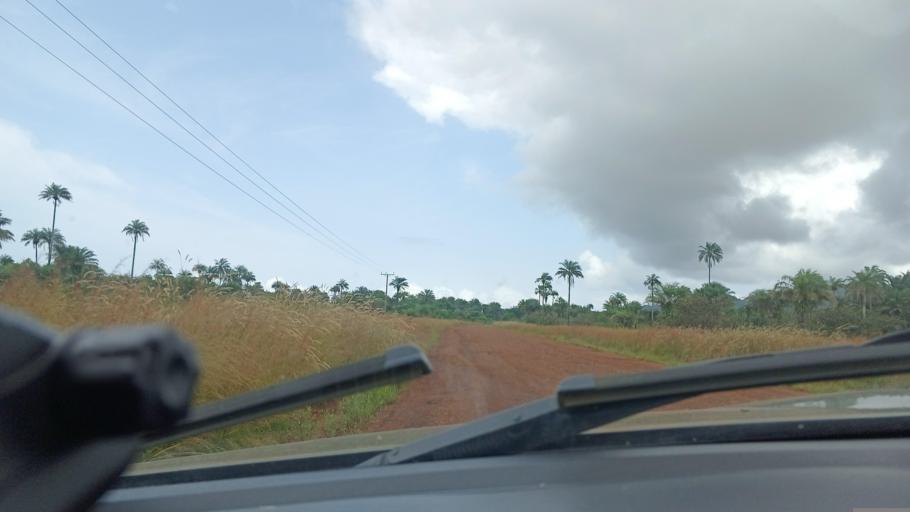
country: LR
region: Grand Cape Mount
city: Robertsport
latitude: 6.7030
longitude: -11.3182
